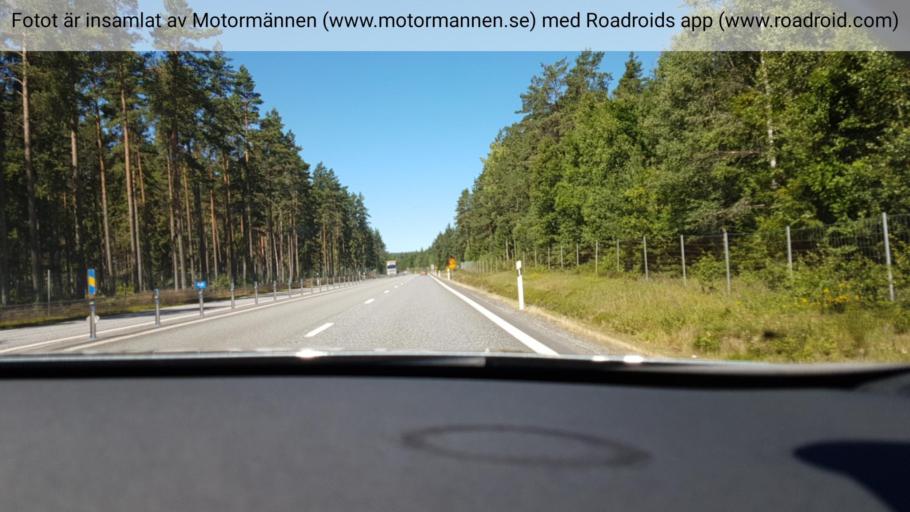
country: SE
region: Joenkoeping
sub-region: Mullsjo Kommun
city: Mullsjoe
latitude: 57.7674
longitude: 13.8142
